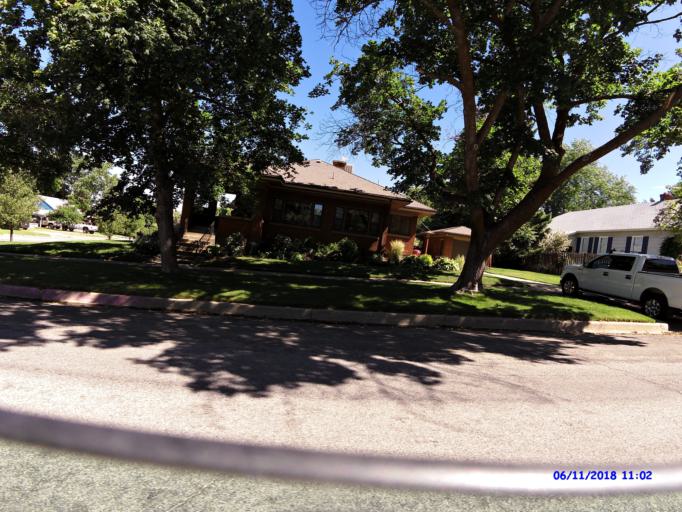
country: US
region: Utah
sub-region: Weber County
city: Ogden
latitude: 41.2181
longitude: -111.9425
